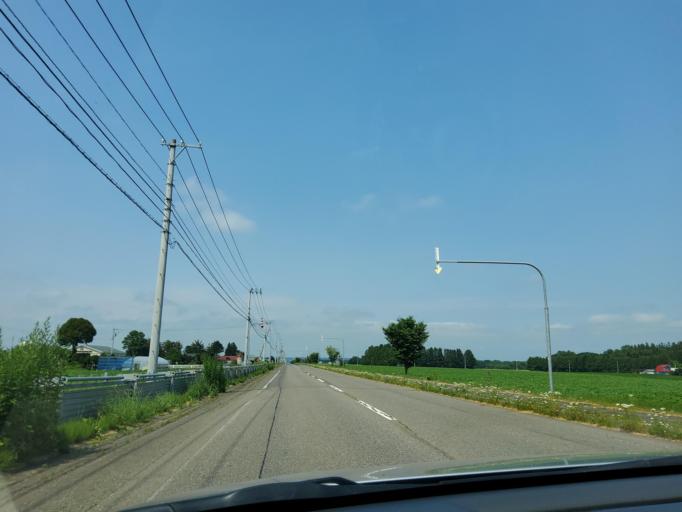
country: JP
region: Hokkaido
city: Obihiro
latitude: 42.8741
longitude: 143.0267
